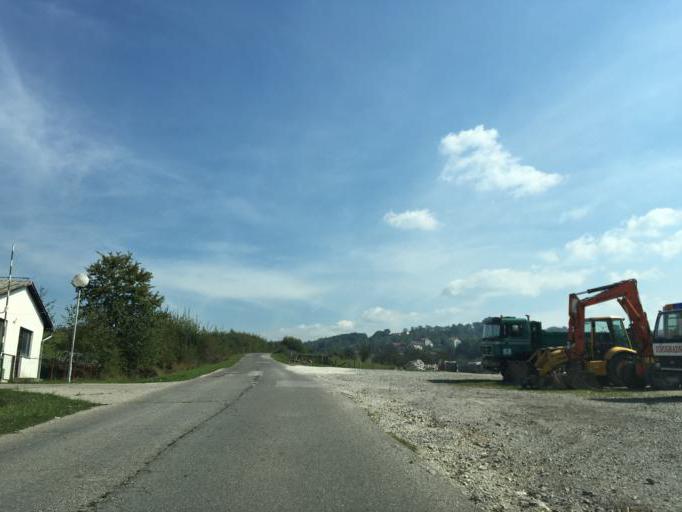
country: BA
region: Federation of Bosnia and Herzegovina
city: Bugojno
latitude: 44.0579
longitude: 17.4664
